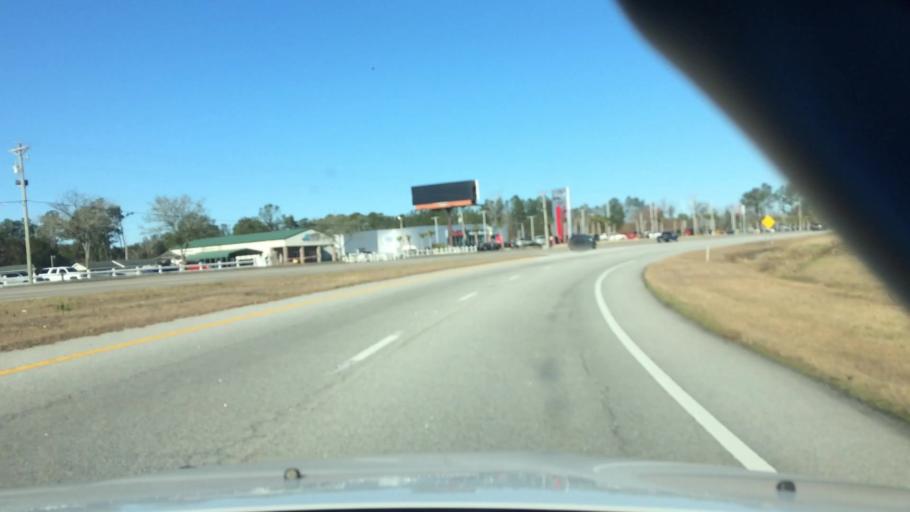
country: US
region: South Carolina
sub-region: Horry County
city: North Myrtle Beach
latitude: 33.8794
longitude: -78.6857
